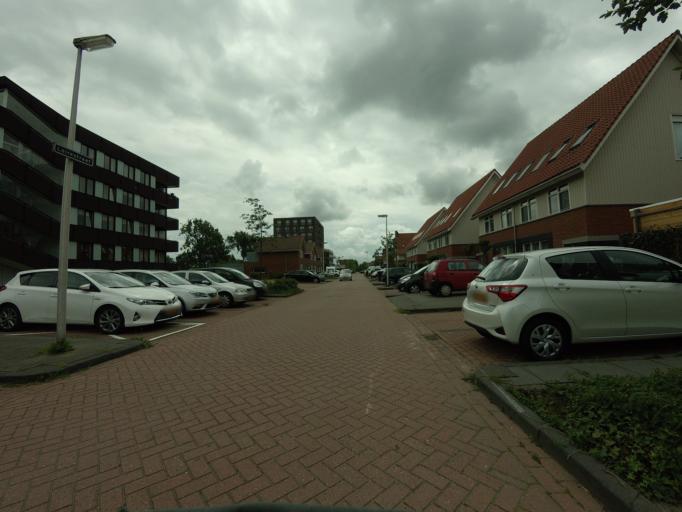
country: NL
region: North Holland
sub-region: Gemeente Purmerend
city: Purmerend
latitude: 52.5023
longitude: 4.9442
